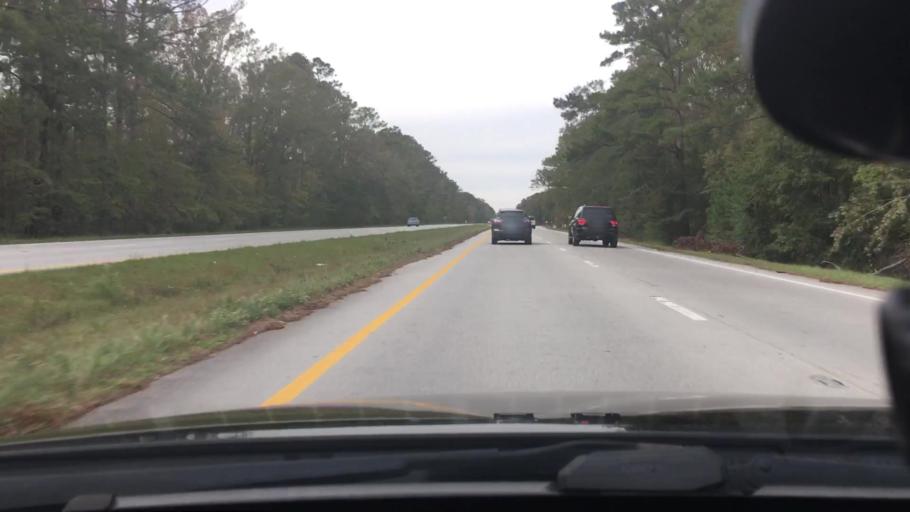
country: US
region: North Carolina
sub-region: Craven County
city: Fairfield Harbour
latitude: 35.0189
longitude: -76.9968
